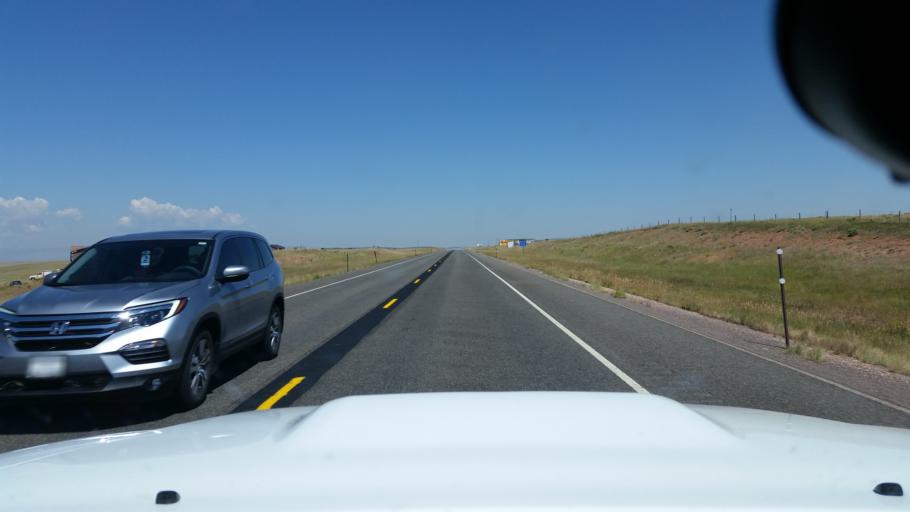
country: US
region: Wyoming
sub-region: Albany County
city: Laramie
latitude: 41.1208
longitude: -105.5449
